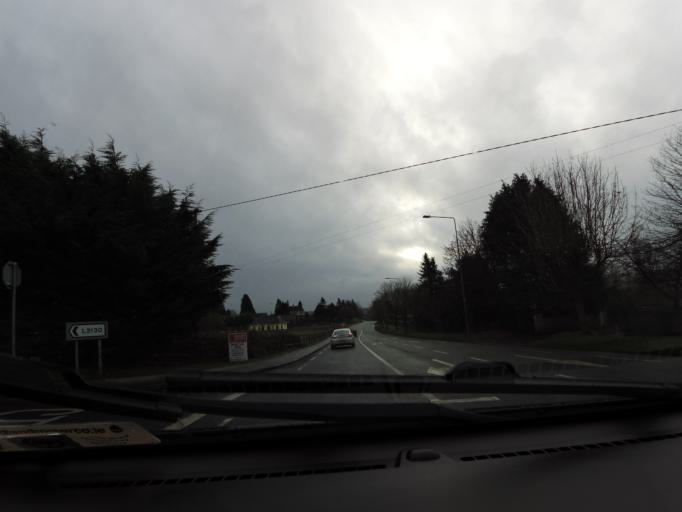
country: IE
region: Munster
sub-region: North Tipperary
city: Roscrea
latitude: 52.9623
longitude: -7.8072
